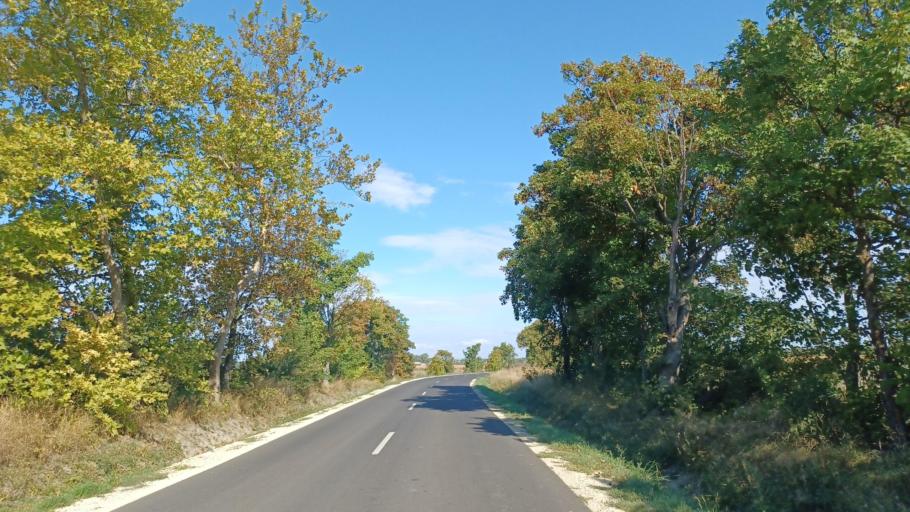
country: HU
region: Tolna
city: Dunaszentgyorgy
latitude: 46.5034
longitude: 18.8244
